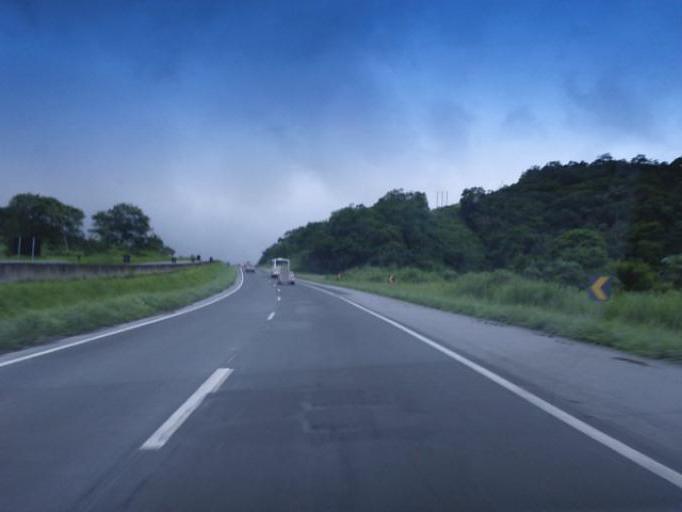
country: BR
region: Sao Paulo
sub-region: Miracatu
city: Miracatu
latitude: -24.3017
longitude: -47.4853
